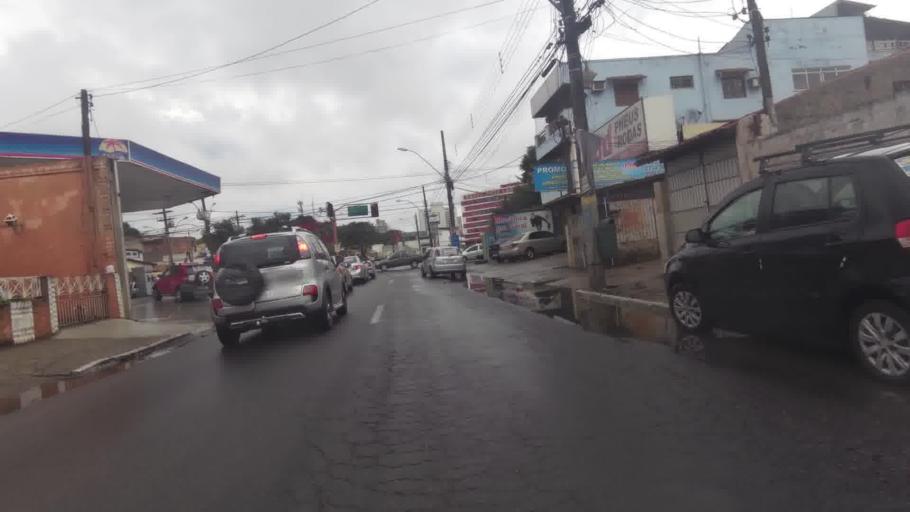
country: BR
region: Rio de Janeiro
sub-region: Campos Dos Goytacazes
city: Campos
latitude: -21.7485
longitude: -41.3365
